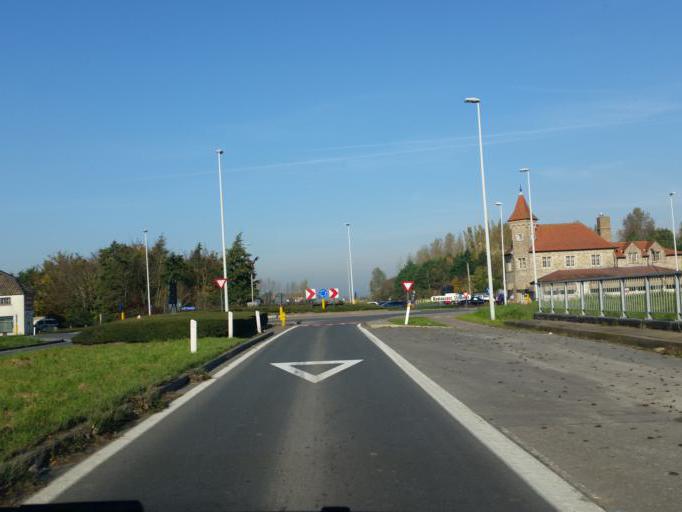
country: BE
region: Flanders
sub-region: Provincie West-Vlaanderen
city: De Haan
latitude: 51.2319
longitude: 3.0607
